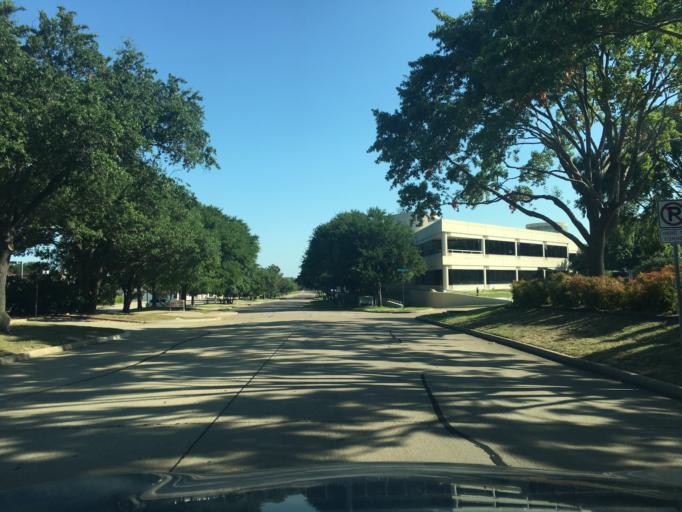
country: US
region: Texas
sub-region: Dallas County
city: Addison
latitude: 32.9633
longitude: -96.8448
